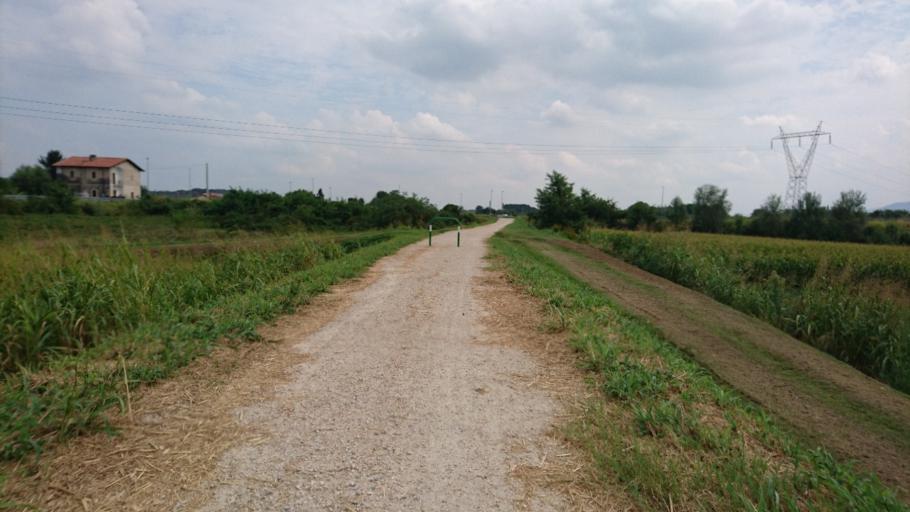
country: IT
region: Veneto
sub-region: Provincia di Vicenza
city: Villaganzerla
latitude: 45.4601
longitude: 11.6426
